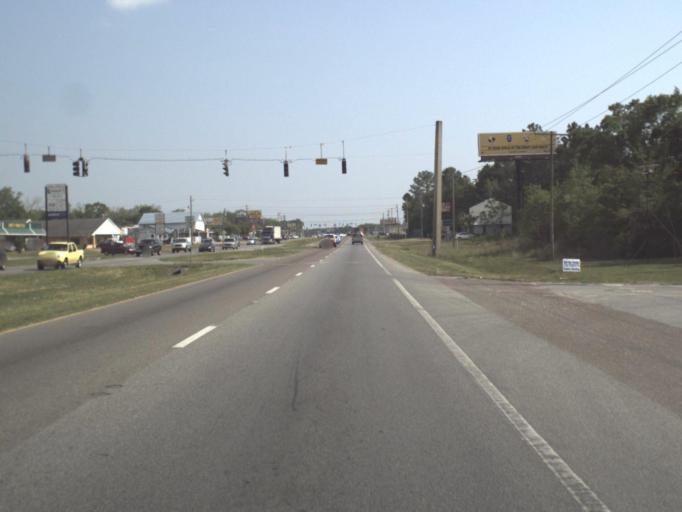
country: US
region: Florida
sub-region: Escambia County
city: Ensley
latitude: 30.5233
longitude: -87.2741
